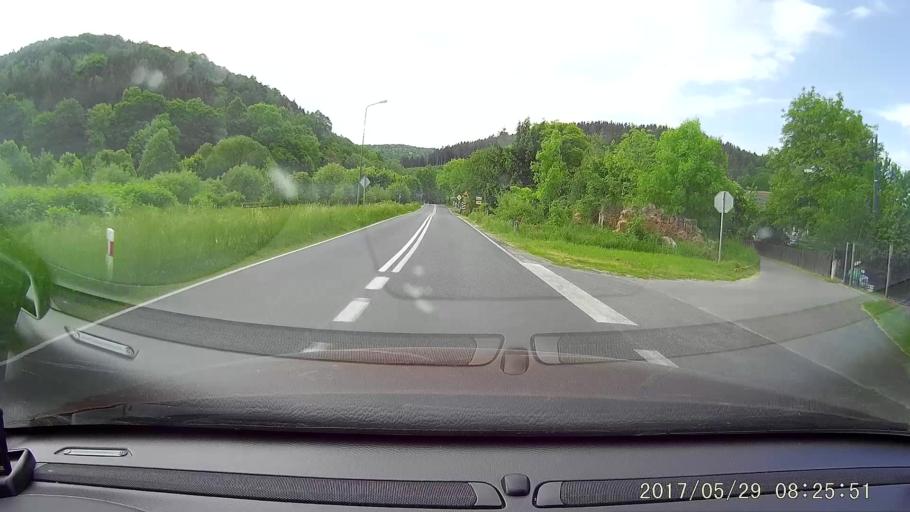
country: PL
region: Lower Silesian Voivodeship
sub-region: Powiat zlotoryjski
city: Swierzawa
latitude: 51.0608
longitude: 15.8633
